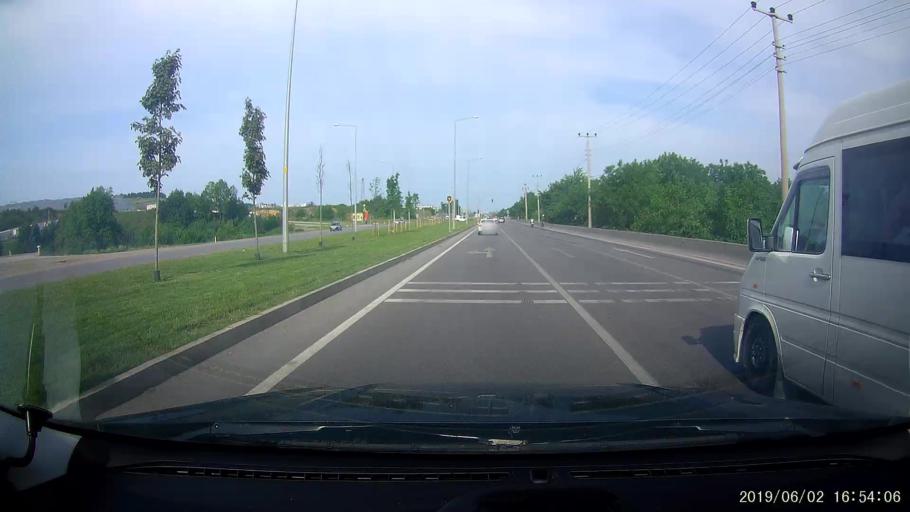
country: TR
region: Samsun
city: Samsun
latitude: 41.2916
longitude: 36.2341
